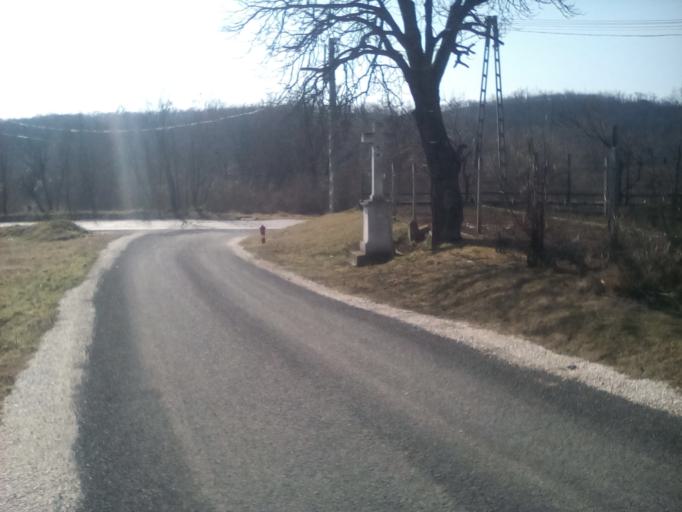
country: HU
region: Pest
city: Soskut
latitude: 47.3981
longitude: 18.8414
